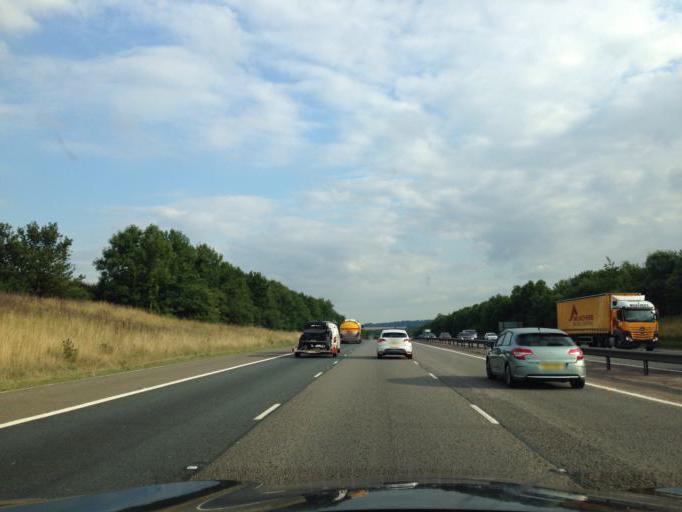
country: GB
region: England
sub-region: Warwickshire
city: Harbury
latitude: 52.1823
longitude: -1.4478
